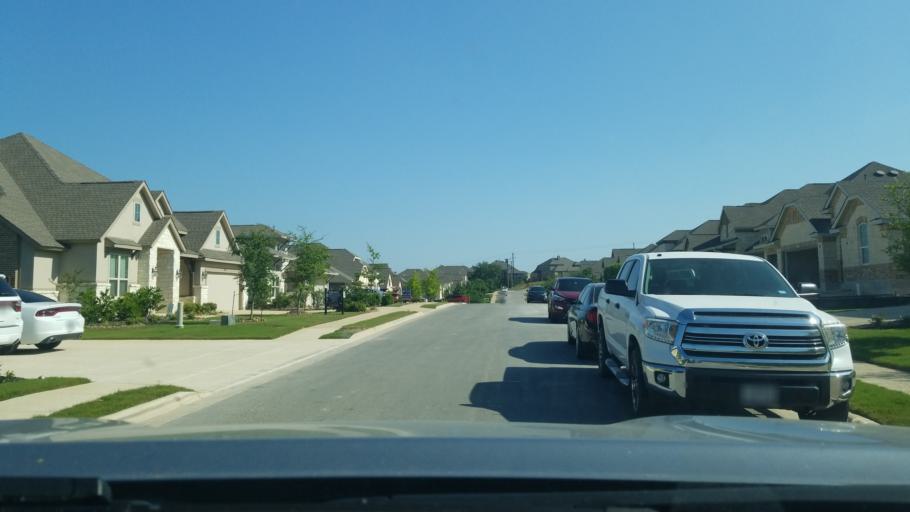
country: US
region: Texas
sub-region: Comal County
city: Bulverde
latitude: 29.7749
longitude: -98.4219
